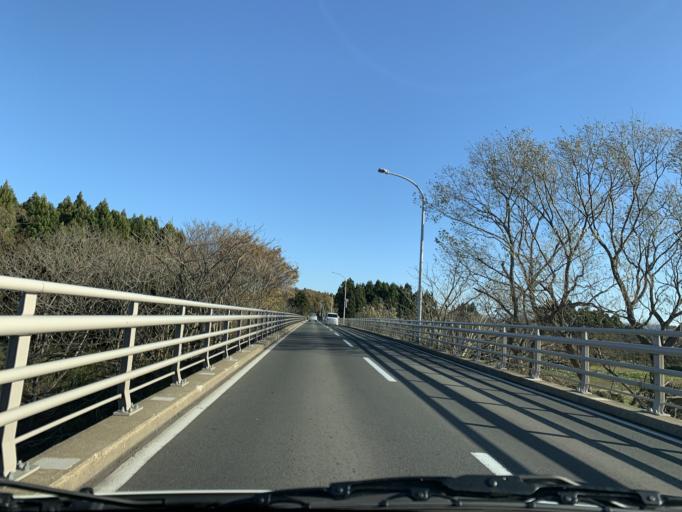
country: JP
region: Iwate
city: Kitakami
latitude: 39.2522
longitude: 141.1160
